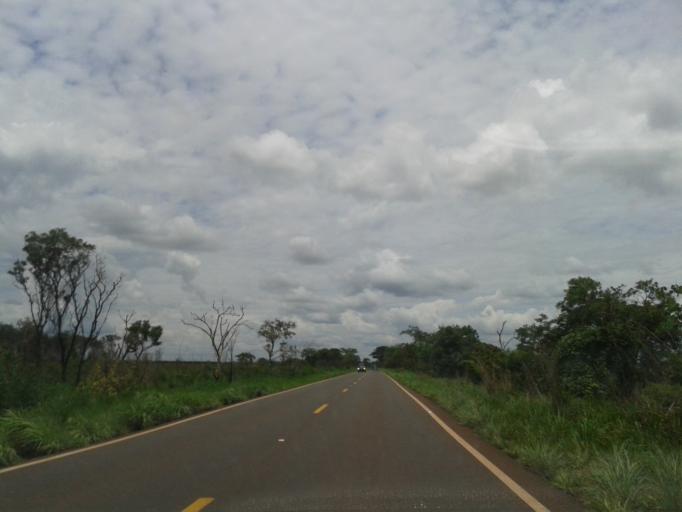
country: BR
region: Minas Gerais
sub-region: Ituiutaba
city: Ituiutaba
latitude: -18.9854
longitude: -49.7959
